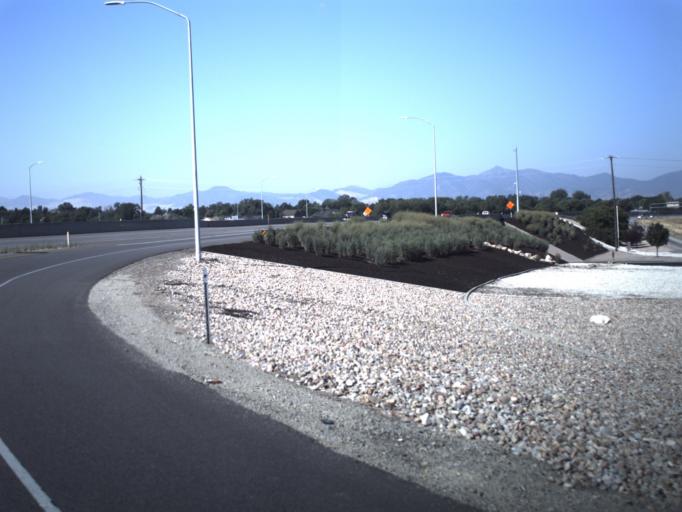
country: US
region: Utah
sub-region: Salt Lake County
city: Taylorsville
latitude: 40.6452
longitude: -111.9370
